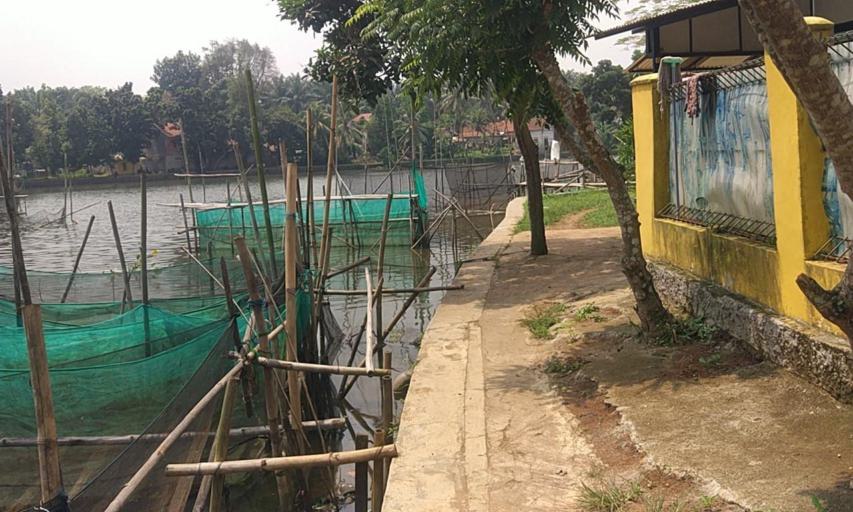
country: ID
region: West Java
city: Ciampea
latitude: -6.5304
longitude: 106.7275
